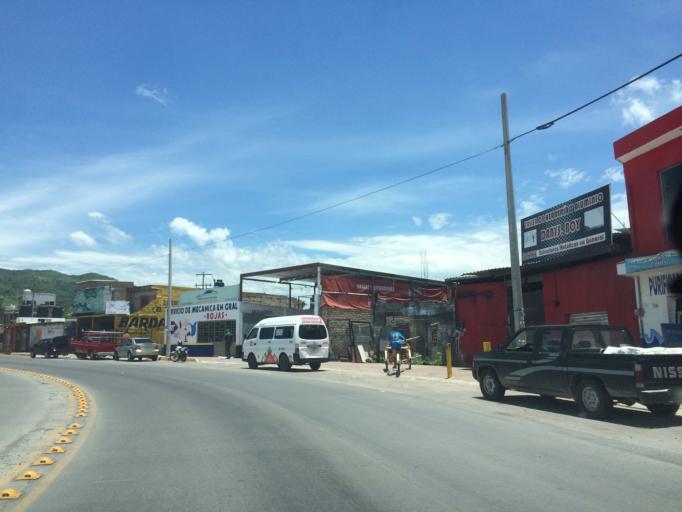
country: MX
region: Nayarit
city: Tepic
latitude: 21.4864
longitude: -104.8663
